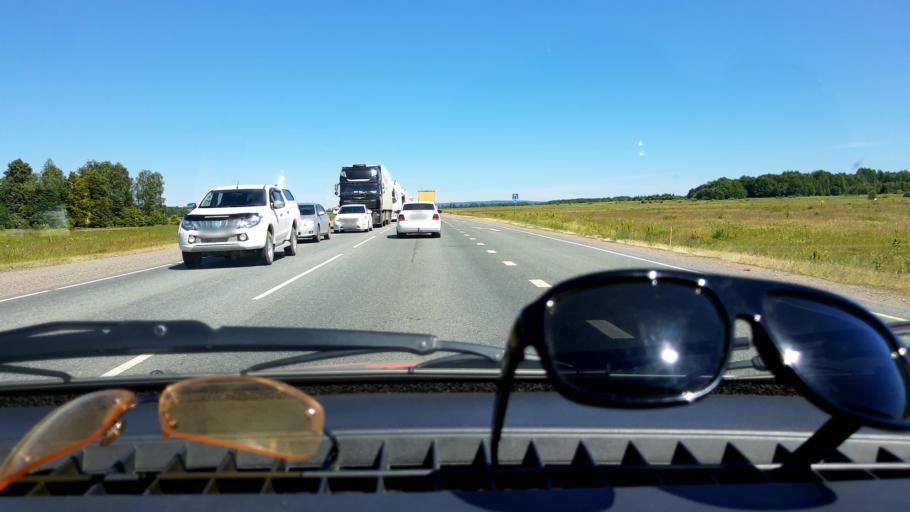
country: RU
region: Bashkortostan
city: Kudeyevskiy
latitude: 54.8174
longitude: 56.7975
